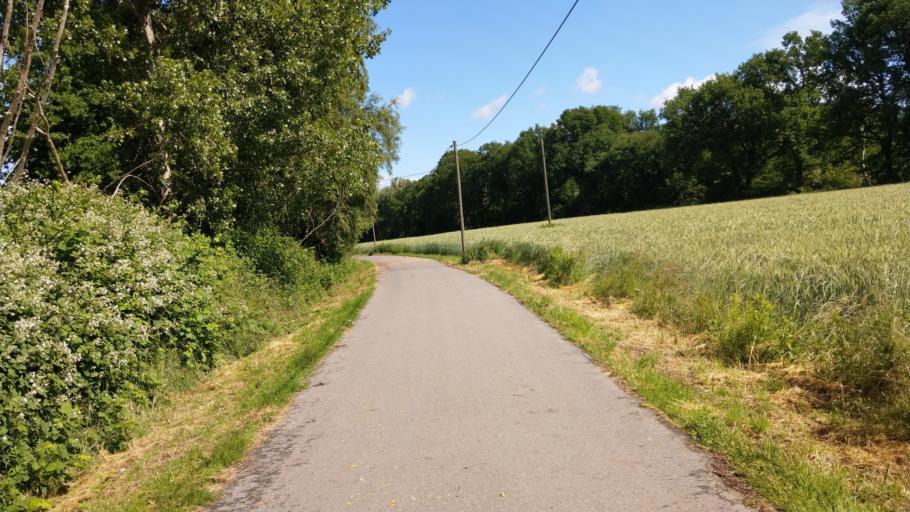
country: DE
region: North Rhine-Westphalia
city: Oer-Erkenschwick
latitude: 51.5870
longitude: 7.2589
